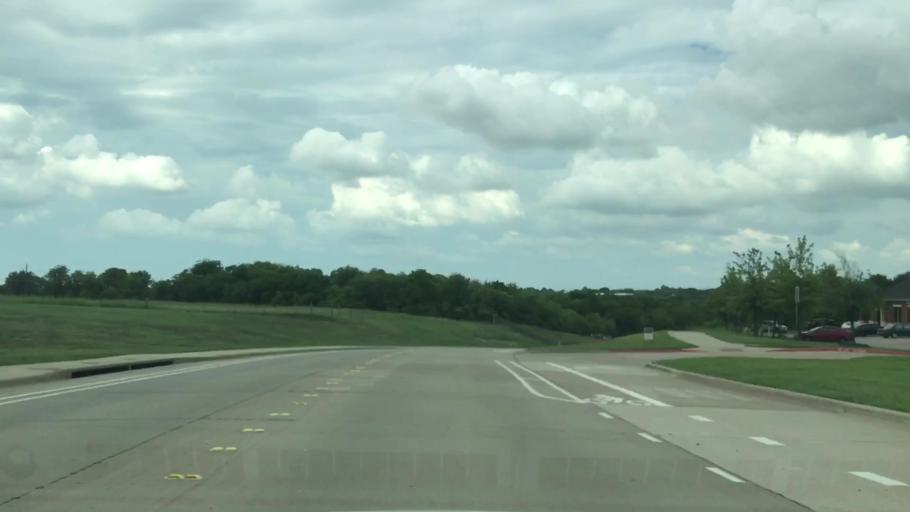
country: US
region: Texas
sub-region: Collin County
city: Frisco
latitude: 33.1361
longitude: -96.8234
